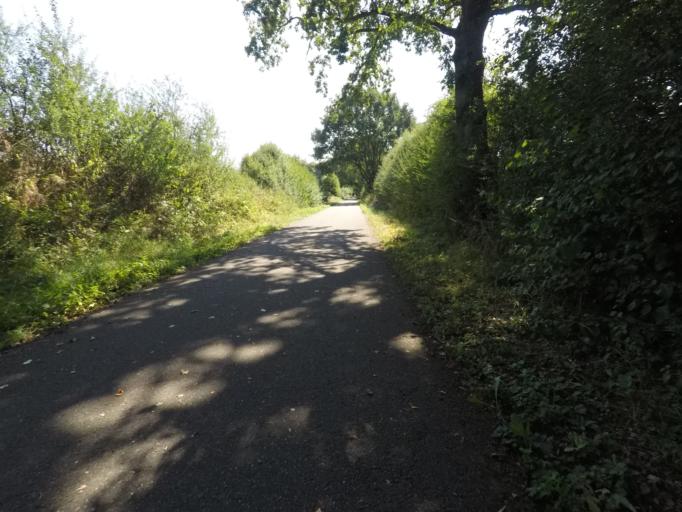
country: LU
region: Luxembourg
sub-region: Canton de Capellen
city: Clemency
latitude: 49.6145
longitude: 5.8768
